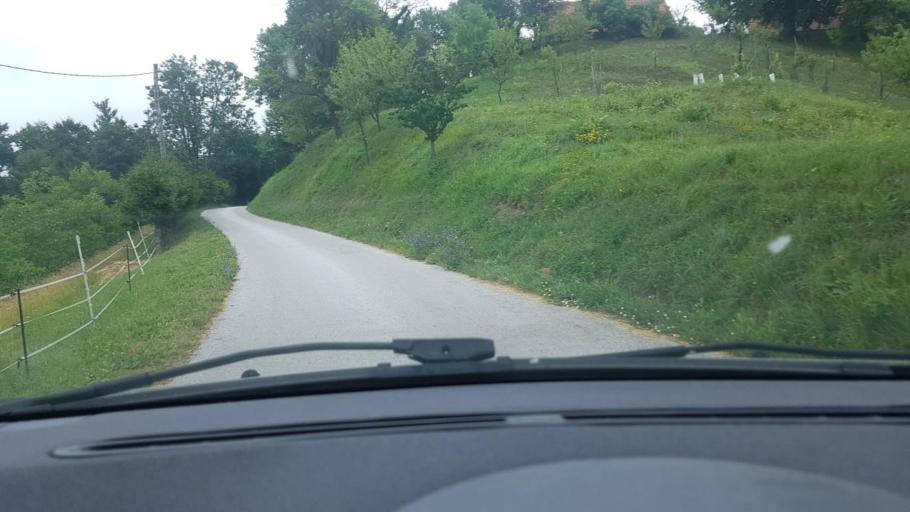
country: SI
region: Videm
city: Videm pri Ptuju
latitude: 46.3350
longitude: 15.9169
